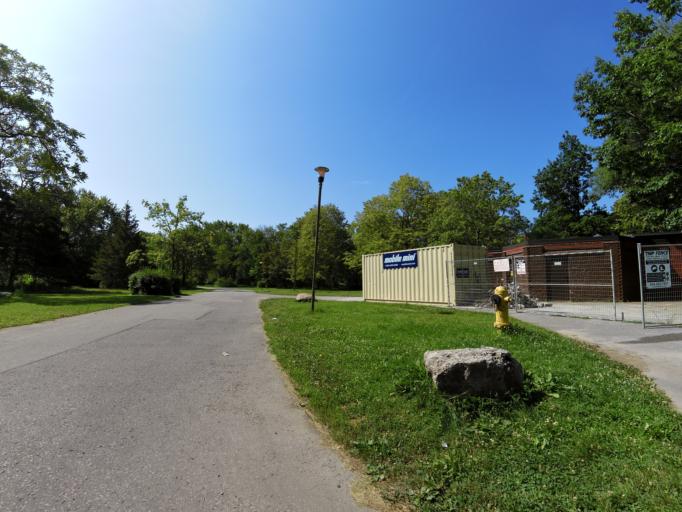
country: CA
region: Ontario
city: Toronto
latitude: 43.6192
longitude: -79.3908
